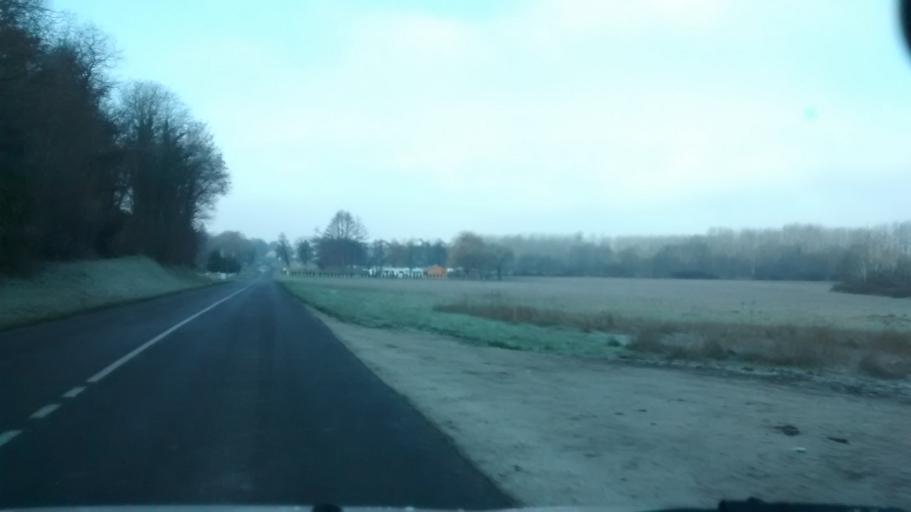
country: FR
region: Centre
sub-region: Departement d'Indre-et-Loire
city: Ballan-Mire
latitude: 47.3565
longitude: 0.5926
